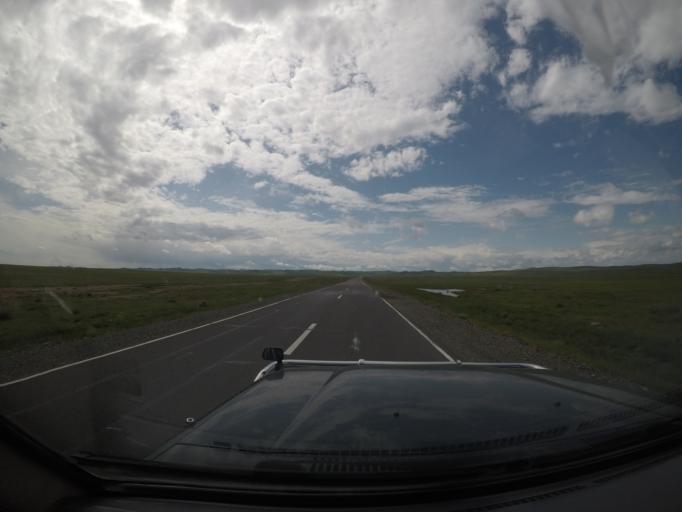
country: MN
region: Hentiy
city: Moron
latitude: 47.4179
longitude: 109.9172
